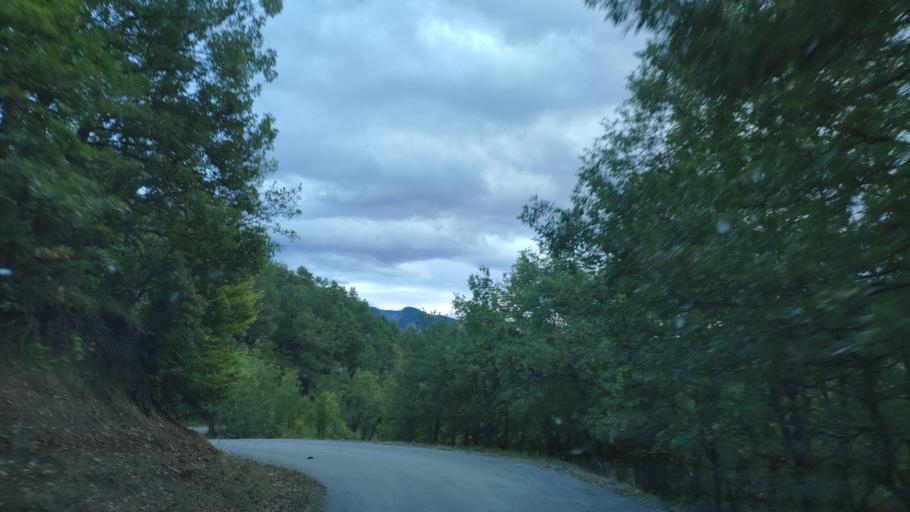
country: AL
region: Korce
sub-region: Rrethi i Kolonjes
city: Erseke
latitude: 40.2506
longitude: 20.8666
